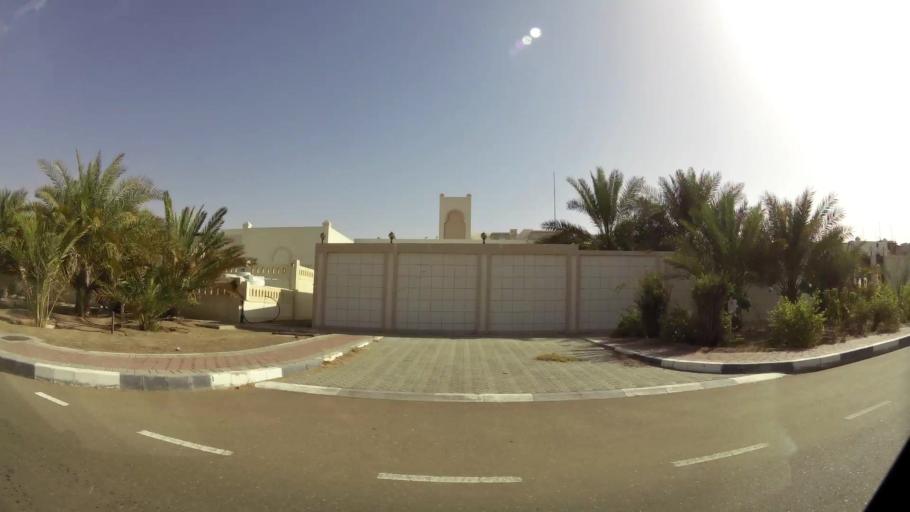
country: OM
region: Al Buraimi
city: Al Buraymi
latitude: 24.3451
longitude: 55.8011
